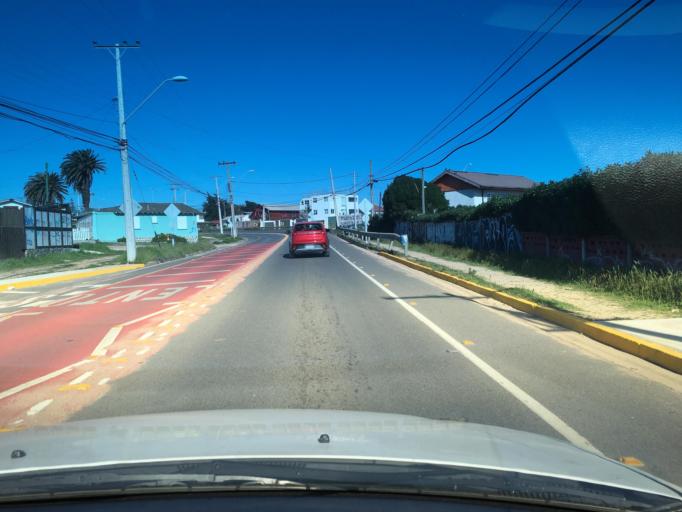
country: CL
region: Valparaiso
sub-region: San Antonio Province
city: El Tabo
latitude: -33.4538
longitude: -71.6722
